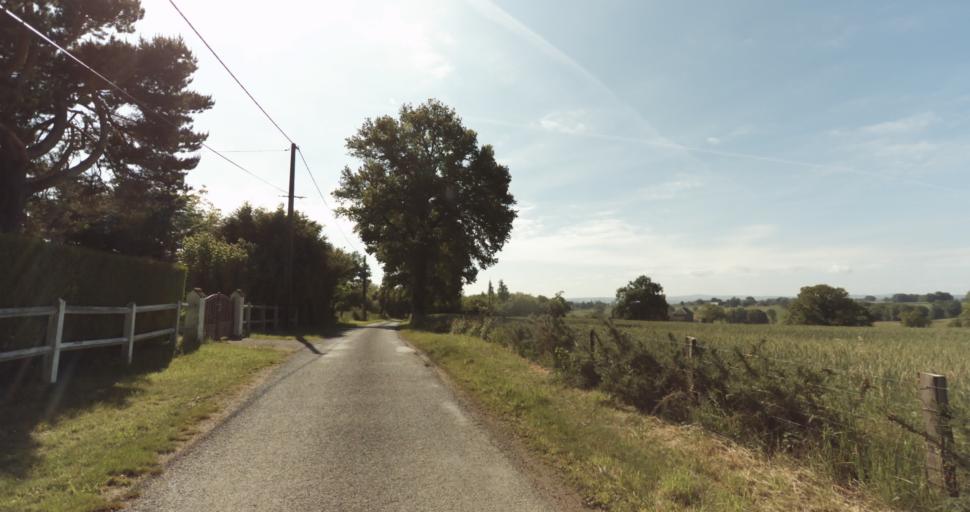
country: FR
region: Limousin
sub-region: Departement de la Haute-Vienne
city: Solignac
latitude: 45.7131
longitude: 1.2656
